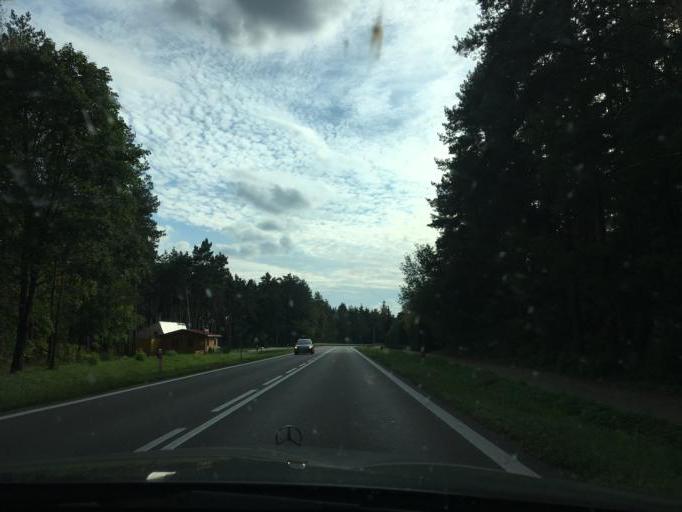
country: PL
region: Podlasie
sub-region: Powiat grajewski
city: Rajgrod
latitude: 53.7101
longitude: 22.6711
